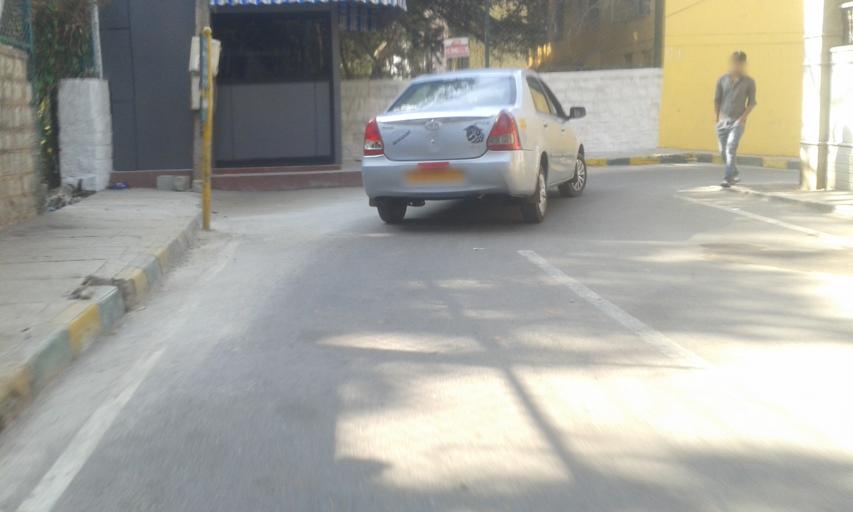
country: IN
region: Karnataka
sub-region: Bangalore Urban
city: Bangalore
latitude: 12.9283
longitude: 77.6116
